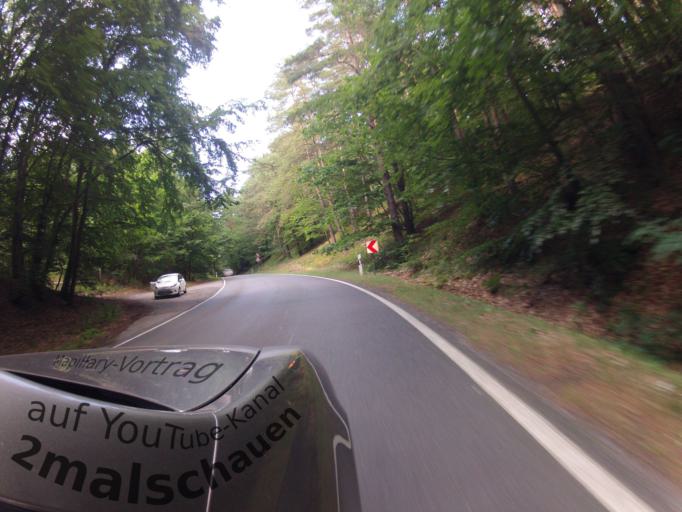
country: DE
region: Mecklenburg-Vorpommern
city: Seebad Heringsdorf
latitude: 53.9284
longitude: 14.1840
